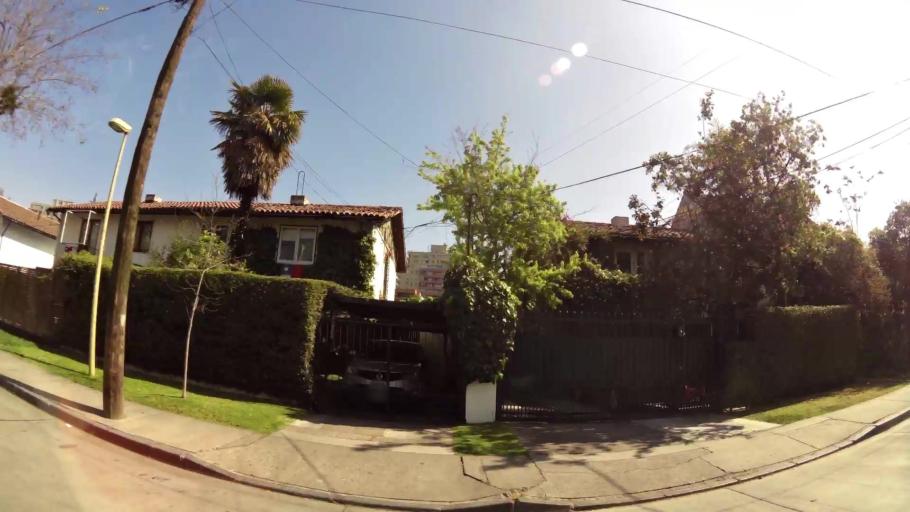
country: CL
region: Santiago Metropolitan
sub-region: Provincia de Santiago
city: Villa Presidente Frei, Nunoa, Santiago, Chile
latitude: -33.4196
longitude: -70.5790
